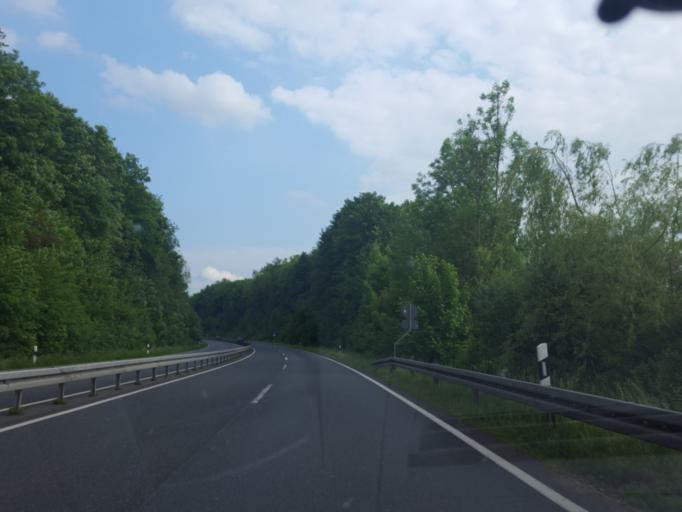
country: DE
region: Lower Saxony
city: Gittelde
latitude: 51.8057
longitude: 10.1881
